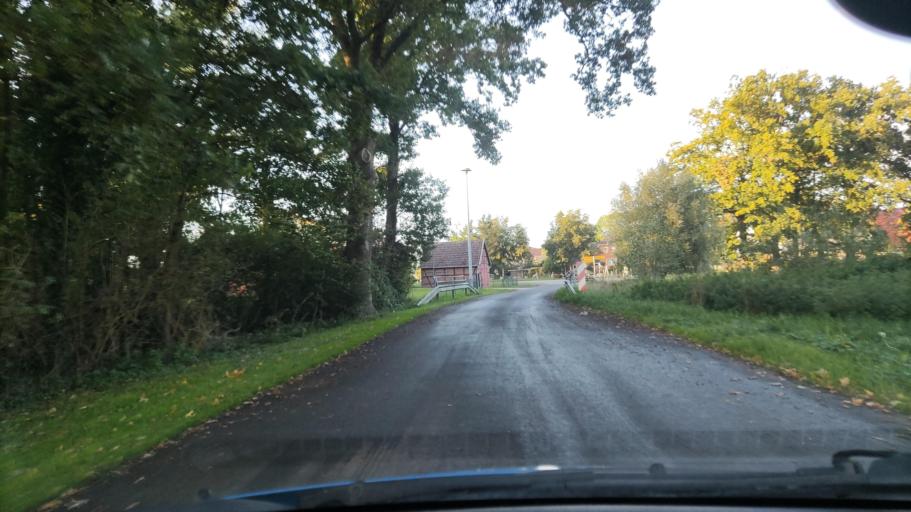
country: DE
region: Lower Saxony
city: Neu Darchau
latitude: 53.2870
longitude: 10.8761
